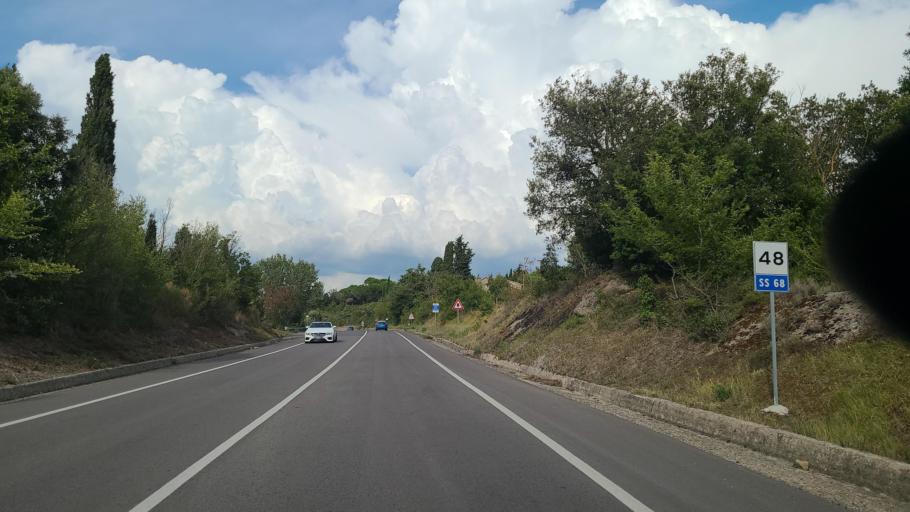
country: IT
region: Tuscany
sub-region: Province of Pisa
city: Volterra
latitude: 43.3901
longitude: 10.9517
